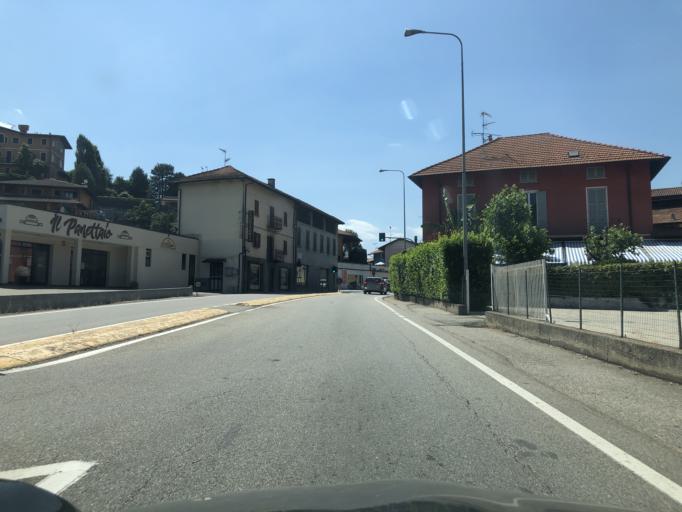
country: IT
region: Piedmont
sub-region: Provincia di Novara
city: Oleggio Castello
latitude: 45.7490
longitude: 8.5312
